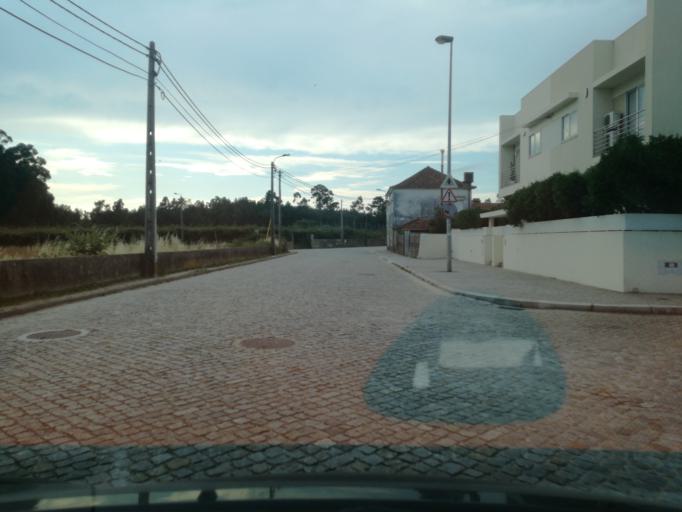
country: PT
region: Porto
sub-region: Maia
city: Maia
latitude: 41.2487
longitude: -8.6085
